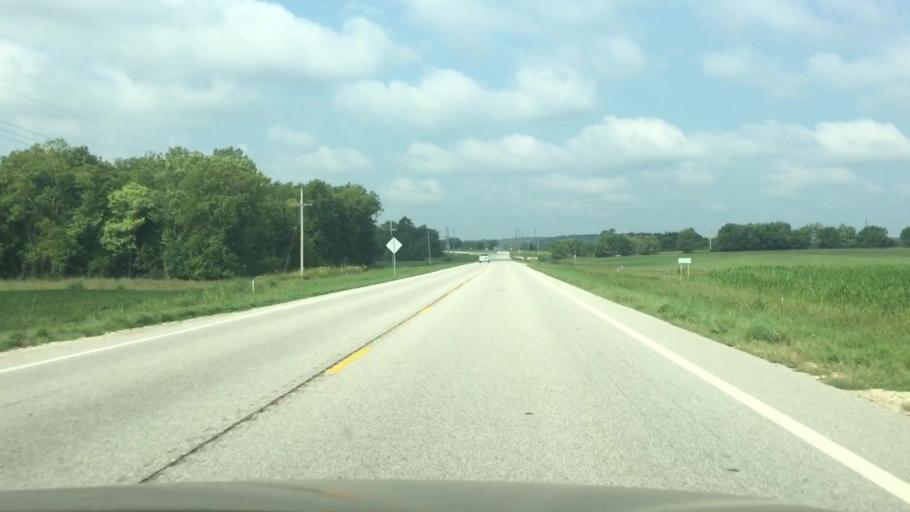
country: US
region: Kansas
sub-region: Anderson County
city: Garnett
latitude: 38.3618
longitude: -95.1332
